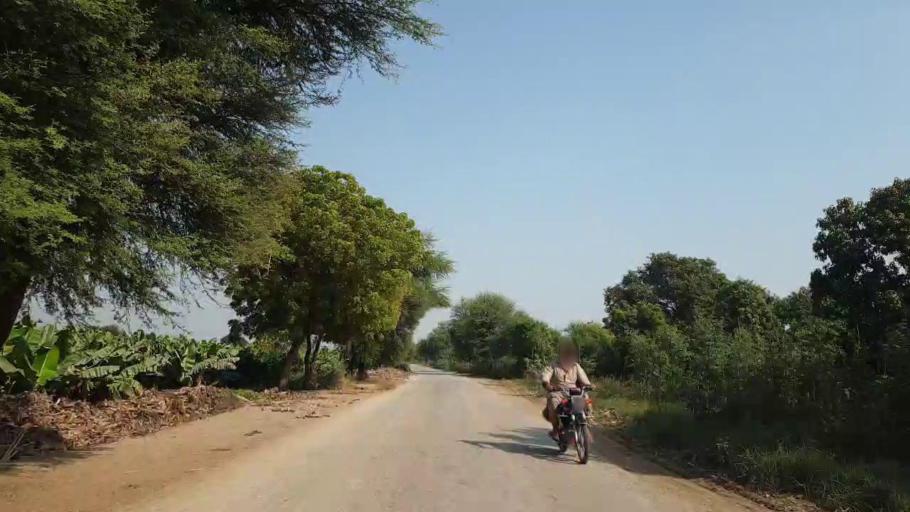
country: PK
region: Sindh
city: Matiari
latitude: 25.5011
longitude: 68.4447
